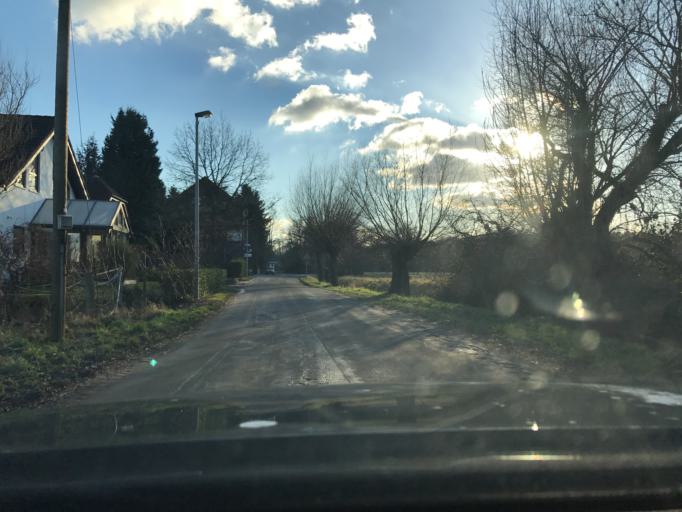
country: DE
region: North Rhine-Westphalia
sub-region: Regierungsbezirk Dusseldorf
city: Krefeld
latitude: 51.3627
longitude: 6.6049
